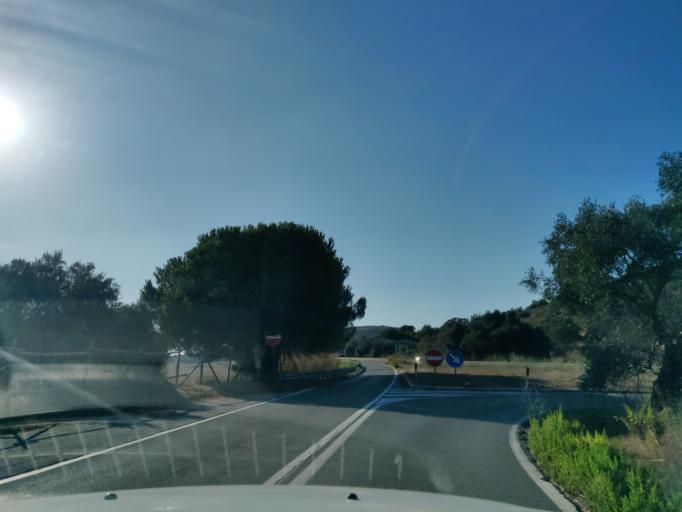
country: IT
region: Tuscany
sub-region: Provincia di Grosseto
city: Orbetello Scalo
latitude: 42.4185
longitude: 11.2960
